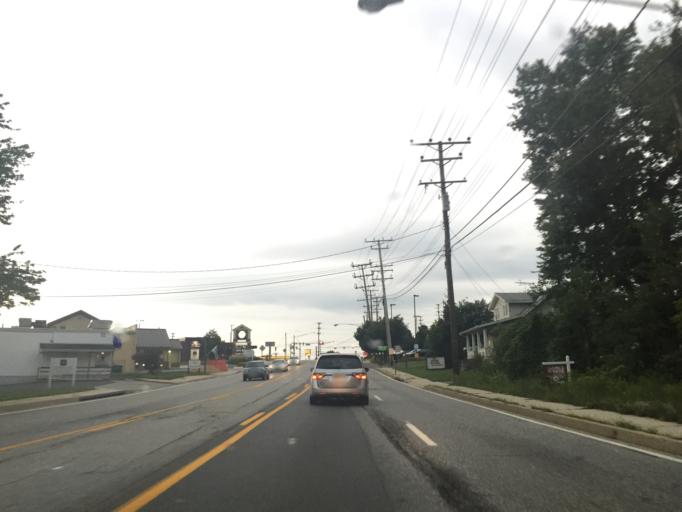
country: US
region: Maryland
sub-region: Baltimore County
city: Carney
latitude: 39.3964
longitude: -76.5222
